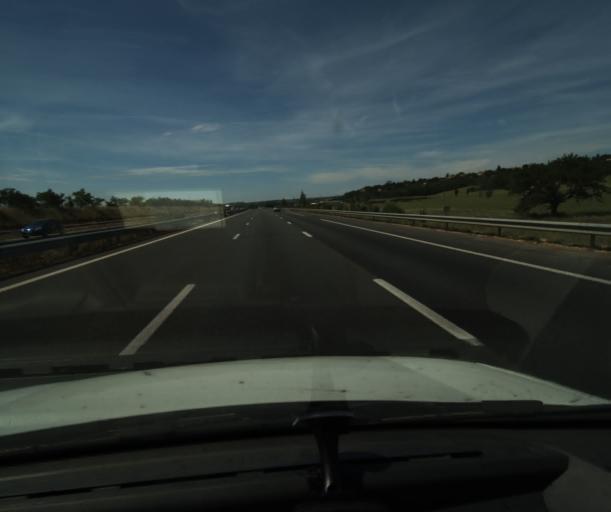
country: FR
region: Midi-Pyrenees
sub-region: Departement de la Haute-Garonne
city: Saint-Sauveur
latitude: 43.7360
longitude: 1.3949
